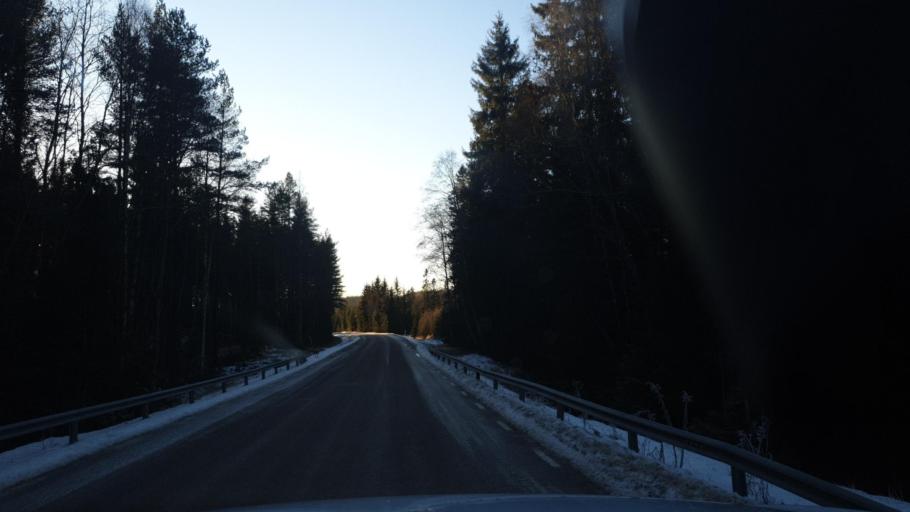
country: SE
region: Vaermland
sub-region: Sunne Kommun
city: Sunne
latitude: 59.8230
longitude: 12.8432
